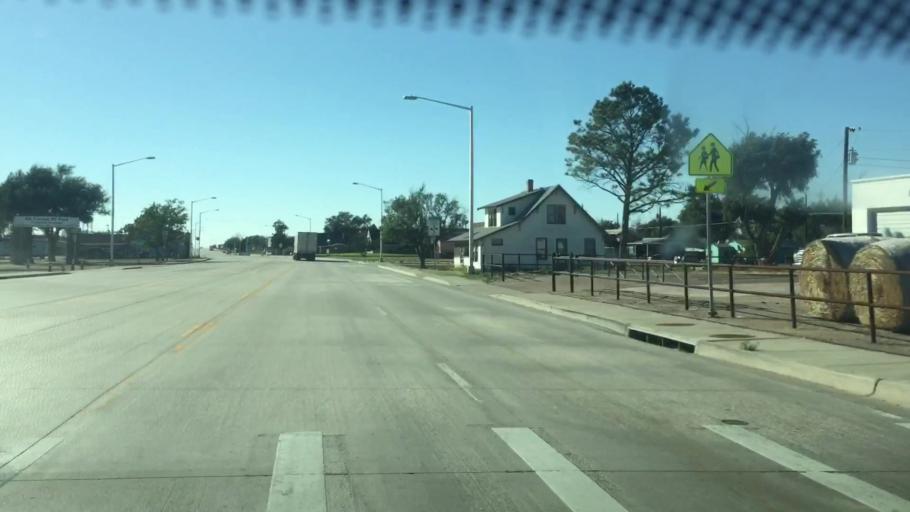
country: US
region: Colorado
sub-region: Kiowa County
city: Eads
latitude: 38.7626
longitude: -102.7888
